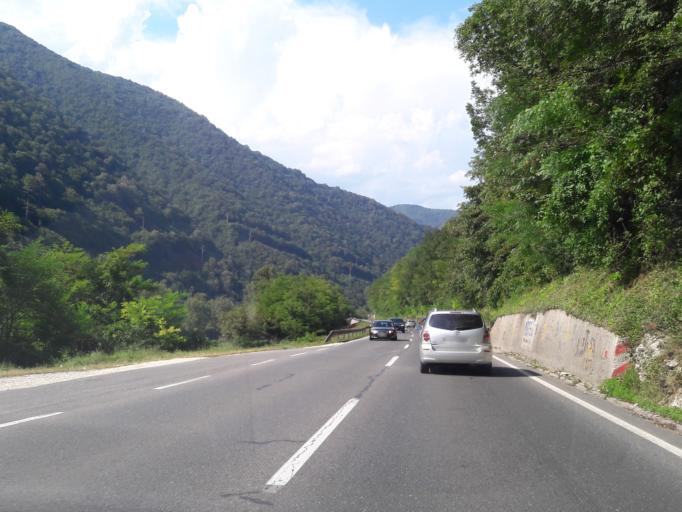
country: BA
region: Federation of Bosnia and Herzegovina
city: Lokvine
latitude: 44.2737
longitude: 17.8817
